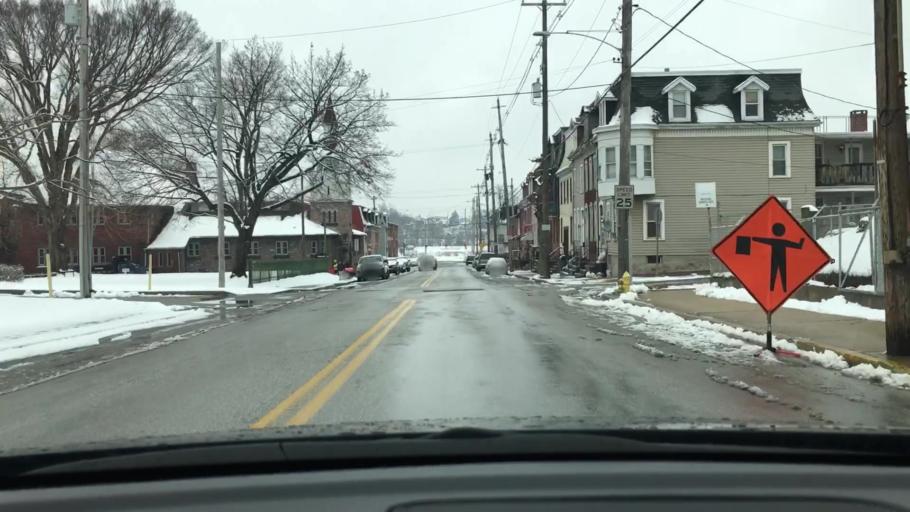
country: US
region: Pennsylvania
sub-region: York County
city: York
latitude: 39.9683
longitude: -76.7262
